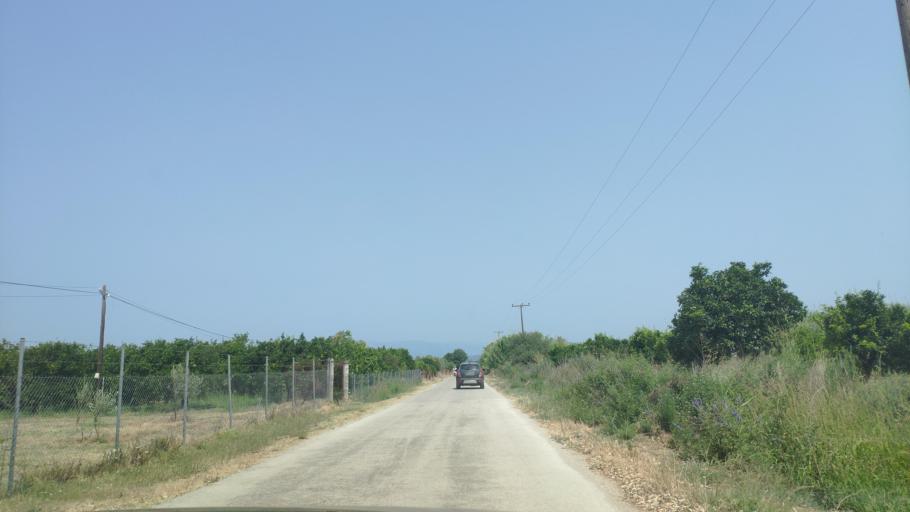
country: GR
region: Epirus
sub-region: Nomos Artas
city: Kompoti
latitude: 39.0549
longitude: 21.0694
